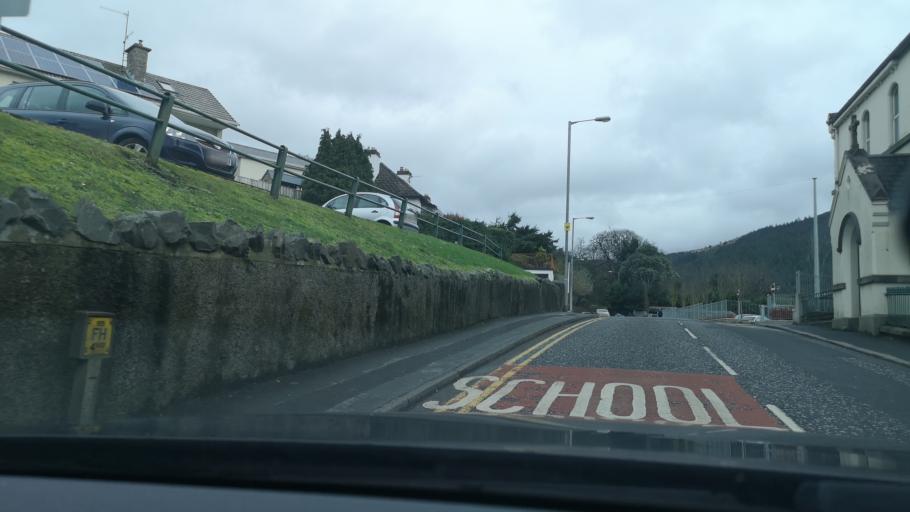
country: GB
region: Northern Ireland
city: Rostrevor
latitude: 54.1027
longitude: -6.1951
